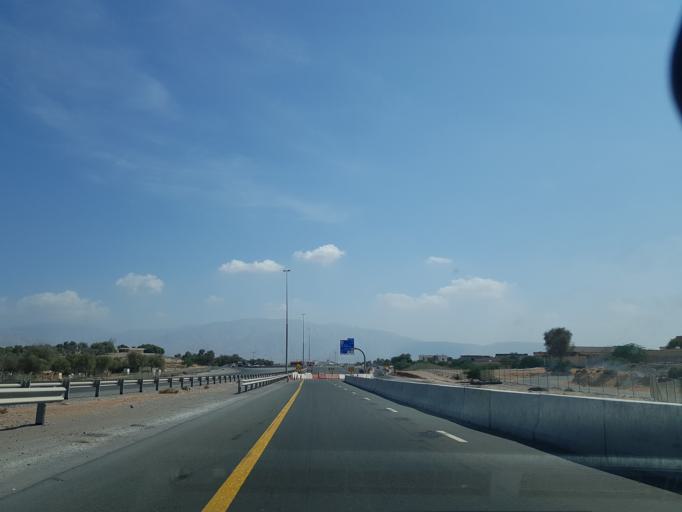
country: AE
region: Ra's al Khaymah
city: Ras al-Khaimah
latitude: 25.7023
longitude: 55.9593
